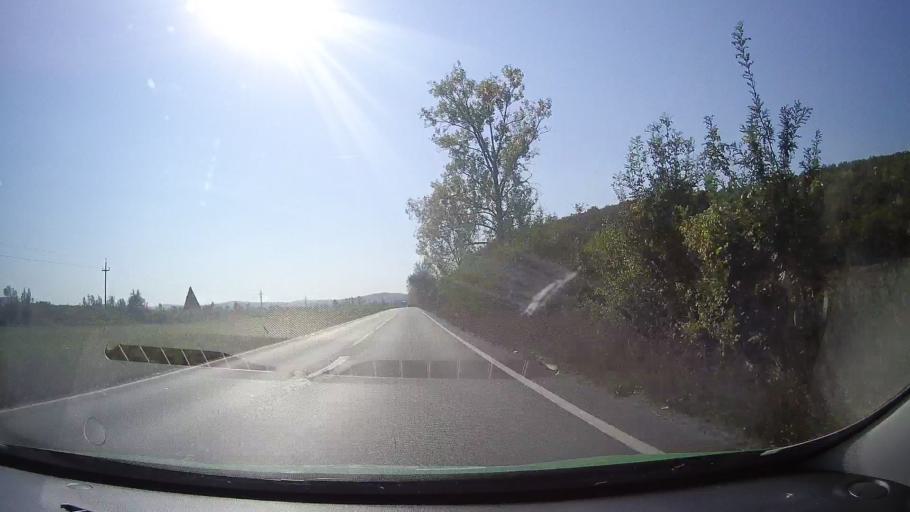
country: RO
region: Arad
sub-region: Comuna Ususau
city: Ususau
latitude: 46.0996
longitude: 21.8143
